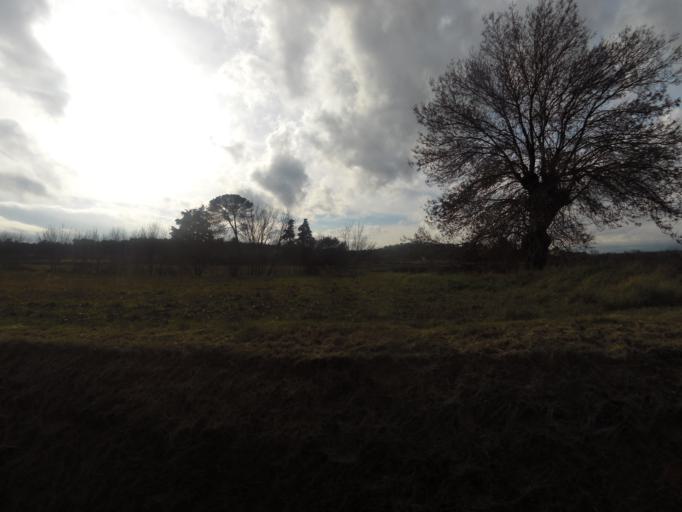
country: FR
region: Languedoc-Roussillon
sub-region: Departement du Gard
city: Saint-Mamert-du-Gard
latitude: 43.8978
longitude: 4.2231
